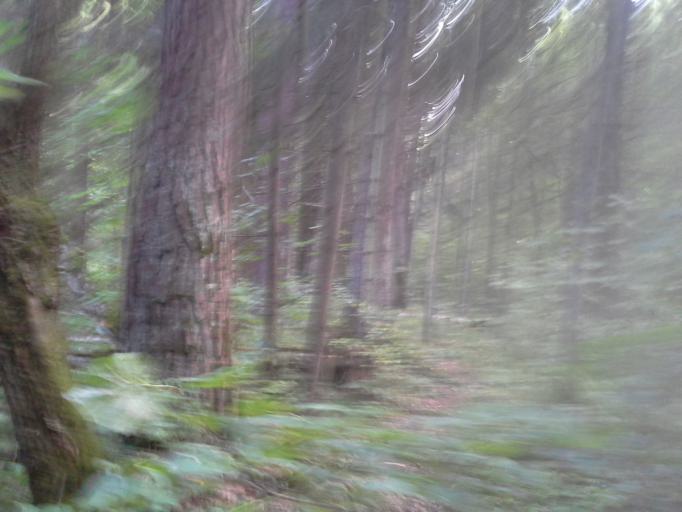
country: RU
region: Moskovskaya
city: Kievskij
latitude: 55.4468
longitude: 36.8564
